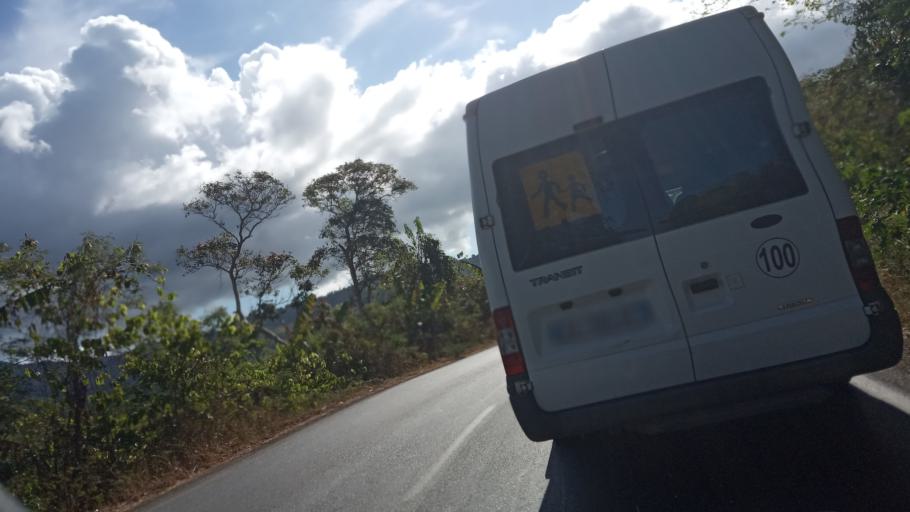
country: YT
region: Dembeni
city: Dembeni
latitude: -12.8369
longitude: 45.1804
